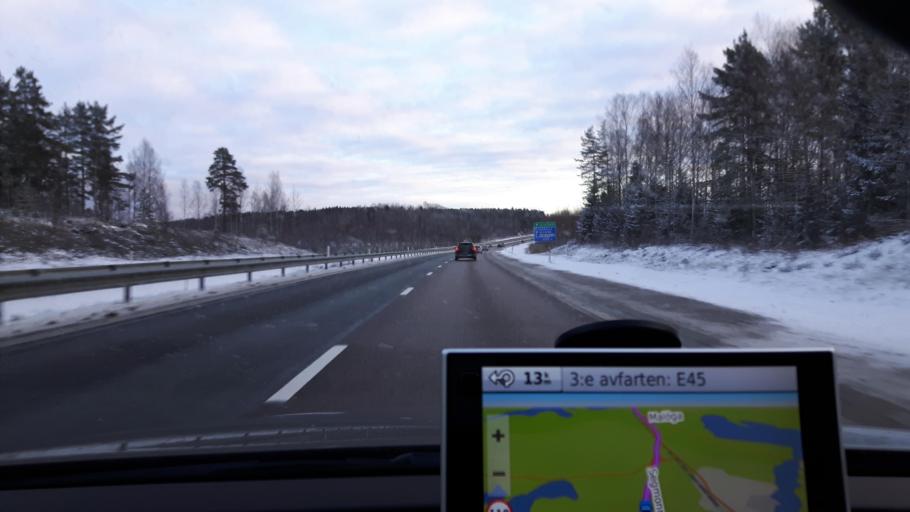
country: SE
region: Vaermland
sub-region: Grums Kommun
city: Slottsbron
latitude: 59.2791
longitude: 13.0224
